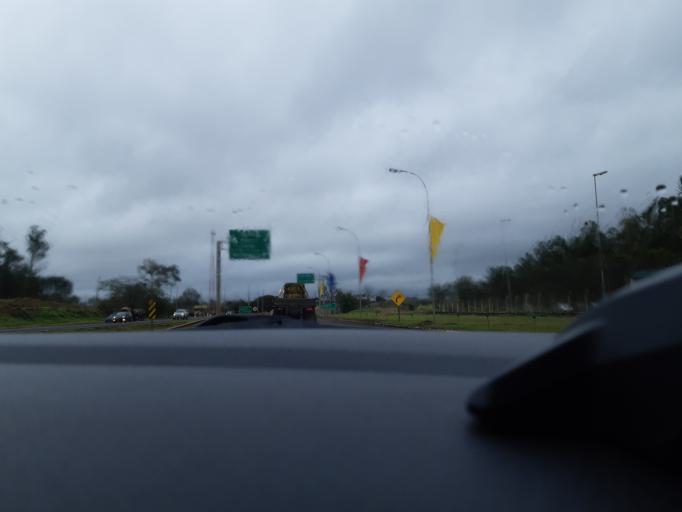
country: BR
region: Sao Paulo
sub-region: Ourinhos
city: Ourinhos
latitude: -22.9804
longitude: -49.9035
